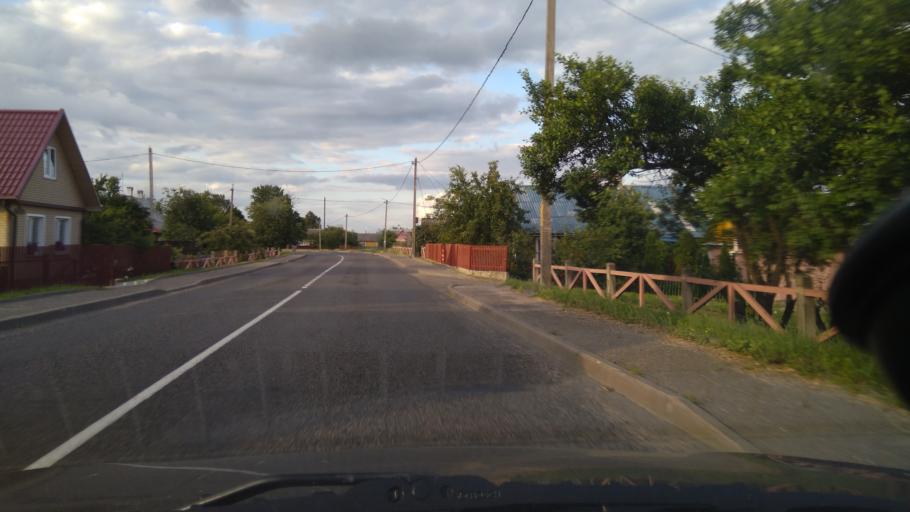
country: BY
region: Grodnenskaya
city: Masty
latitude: 53.4320
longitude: 24.6340
